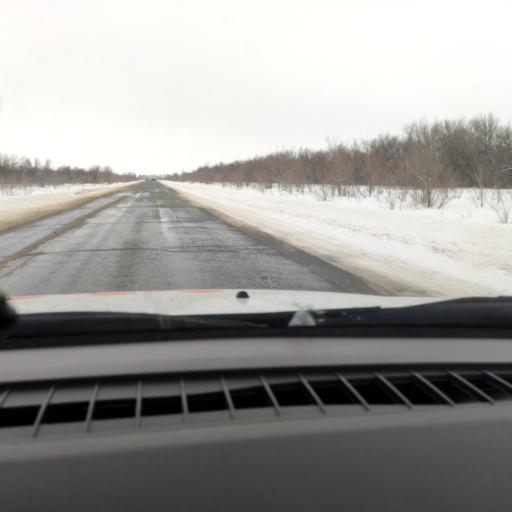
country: RU
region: Samara
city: Mayskoye
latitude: 52.4476
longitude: 50.5258
